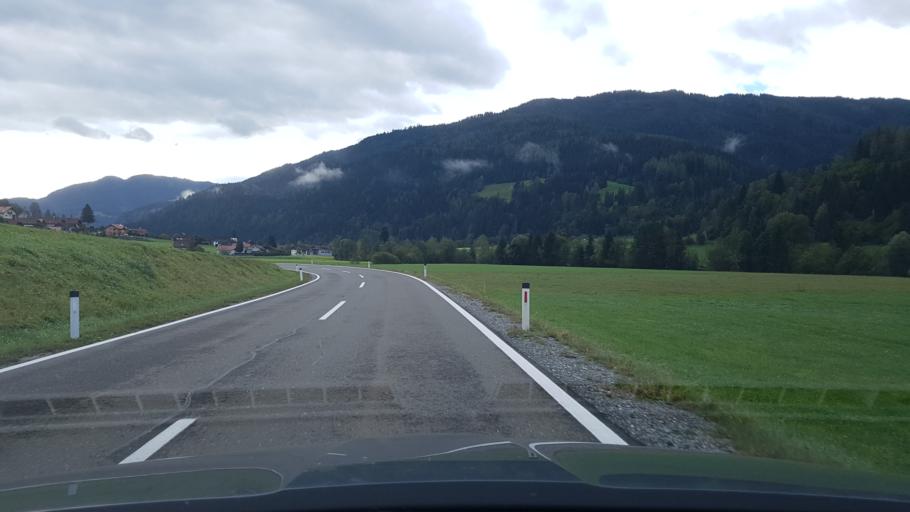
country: AT
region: Styria
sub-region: Politischer Bezirk Murau
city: Winklern bei Oberwolz
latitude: 47.1719
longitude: 14.2353
